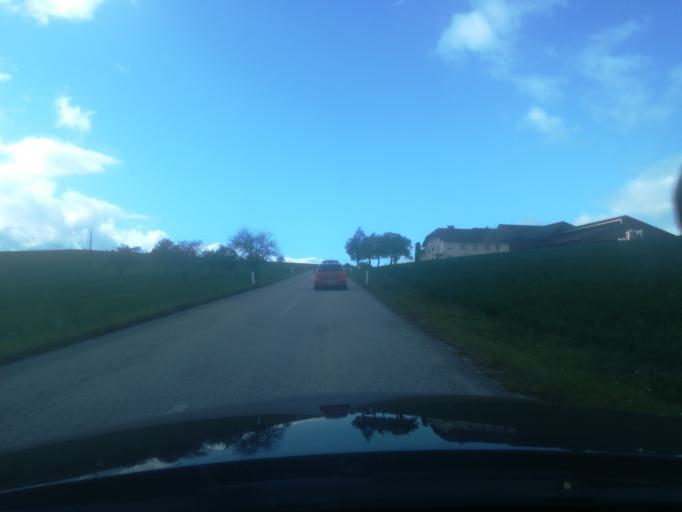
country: AT
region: Upper Austria
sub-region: Politischer Bezirk Urfahr-Umgebung
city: Eidenberg
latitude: 48.3526
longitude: 14.2619
